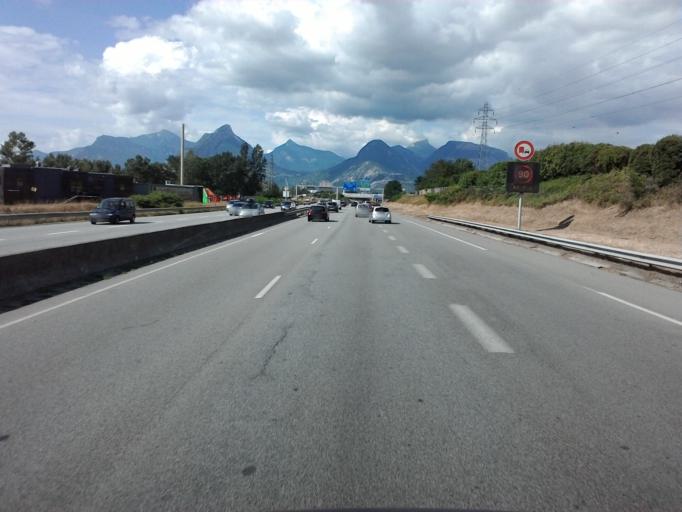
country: FR
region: Rhone-Alpes
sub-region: Departement de l'Isere
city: Seyssins
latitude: 45.1530
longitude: 5.6981
